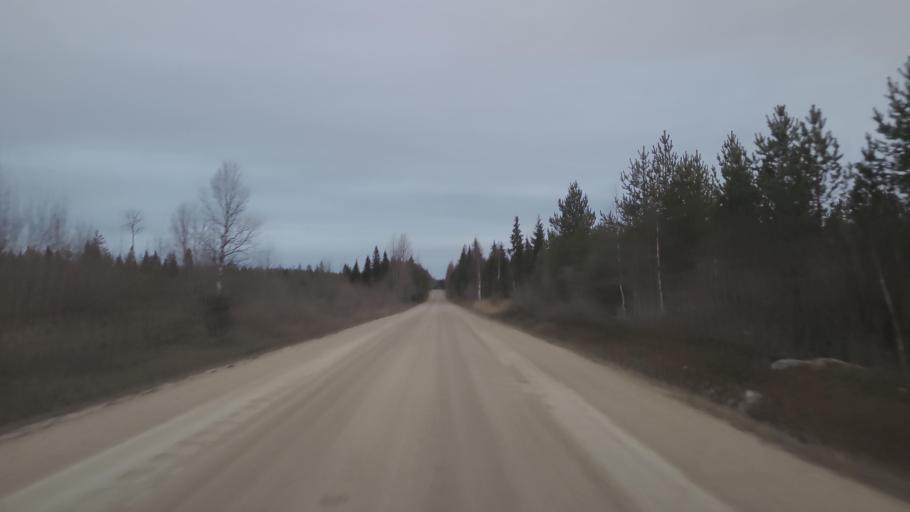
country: FI
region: Lapland
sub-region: Kemi-Tornio
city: Tervola
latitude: 66.0719
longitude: 24.8701
